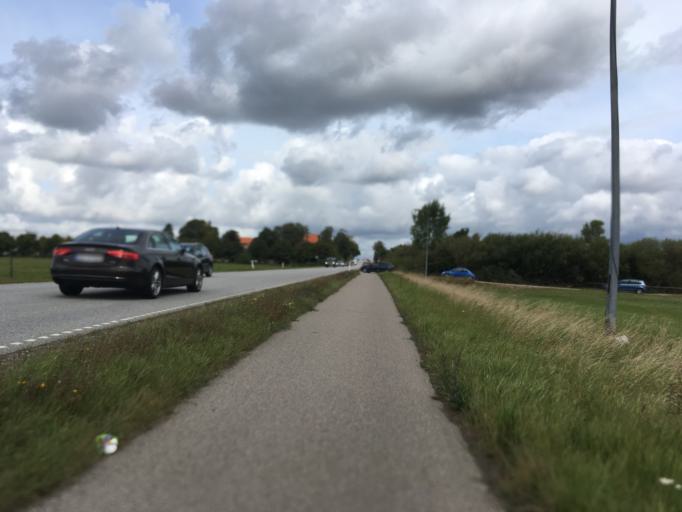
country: DK
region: Capital Region
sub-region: Hillerod Kommune
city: Hillerod
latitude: 55.9116
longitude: 12.2873
